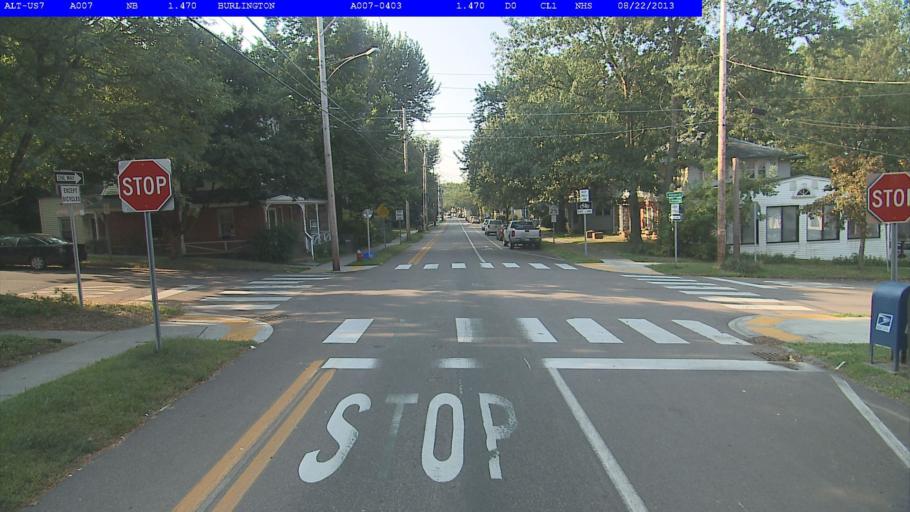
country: US
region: Vermont
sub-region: Chittenden County
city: Burlington
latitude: 44.4724
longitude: -73.2106
